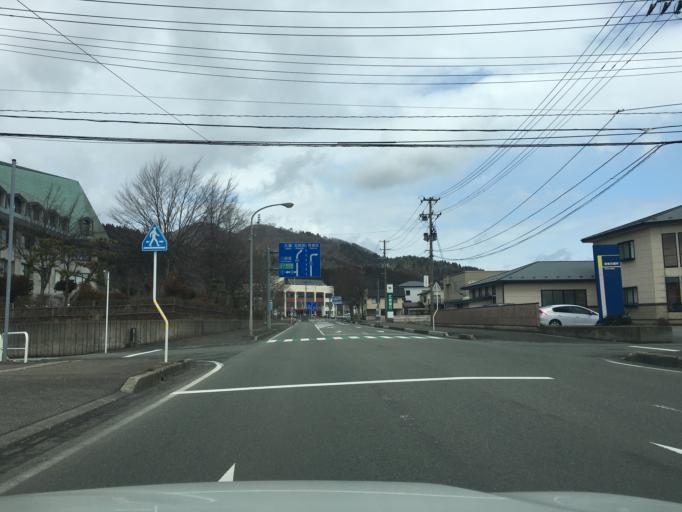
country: JP
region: Akita
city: Tenno
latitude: 39.9430
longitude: 140.1122
